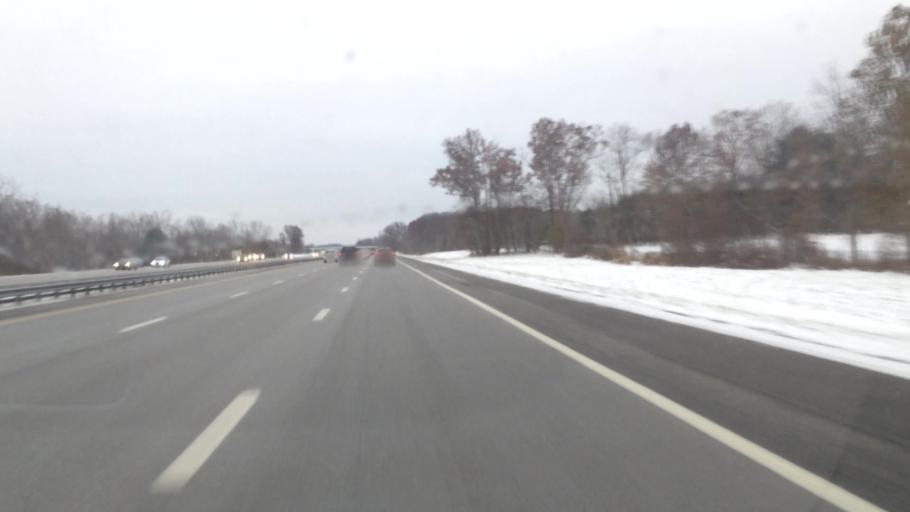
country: US
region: Ohio
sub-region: Cuyahoga County
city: Strongsville
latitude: 41.2847
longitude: -81.8080
